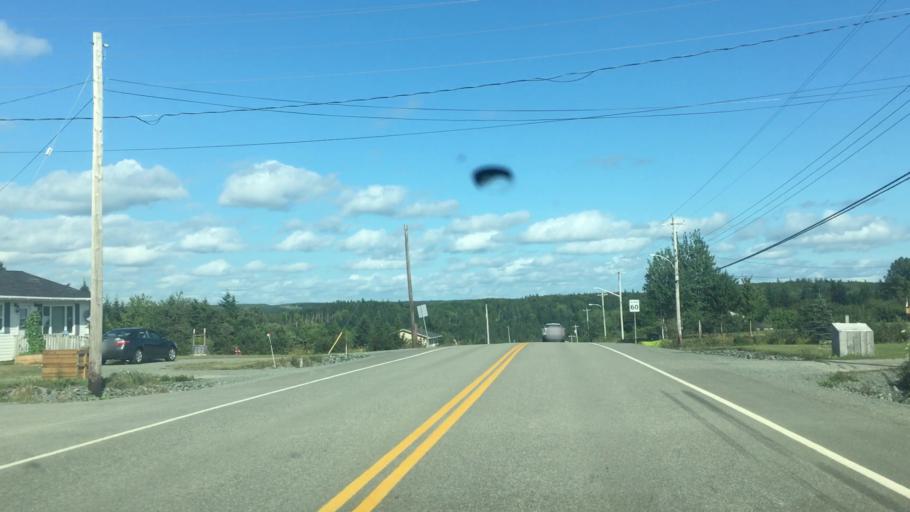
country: CA
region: Nova Scotia
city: Princeville
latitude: 45.6840
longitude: -60.7626
